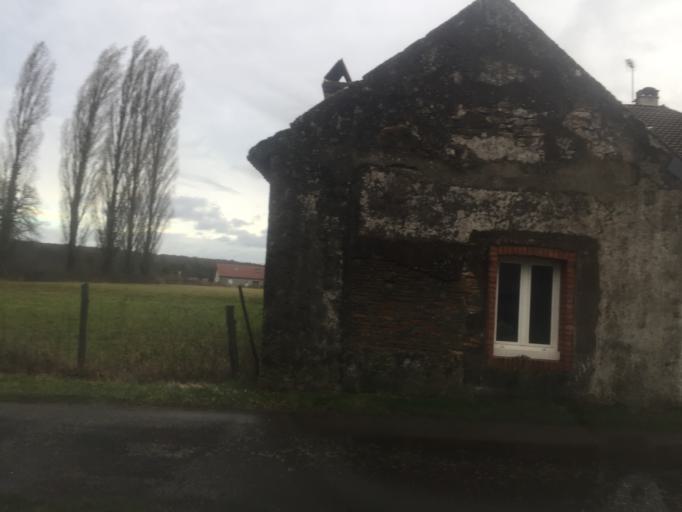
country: FR
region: Franche-Comte
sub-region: Departement de la Haute-Saone
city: Pesmes
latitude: 47.2249
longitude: 5.5001
